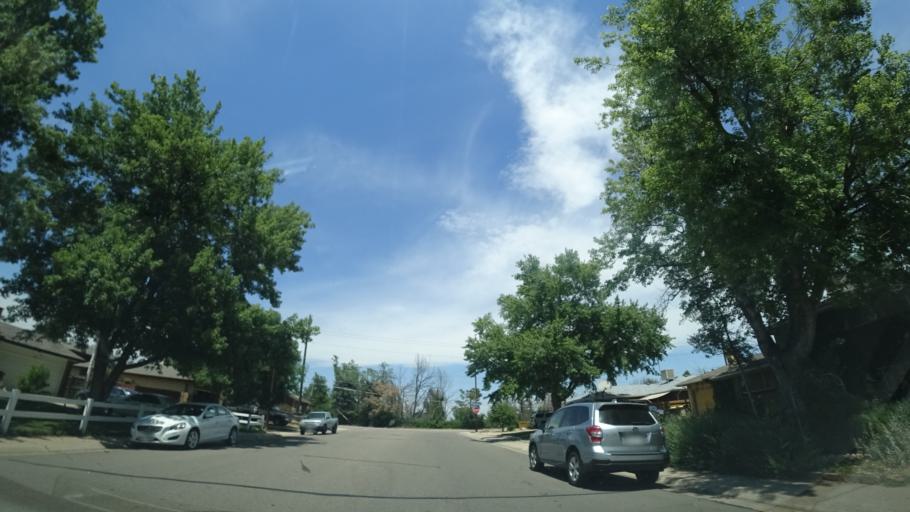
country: US
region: Colorado
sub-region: Jefferson County
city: Lakewood
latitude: 39.6960
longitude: -105.0895
